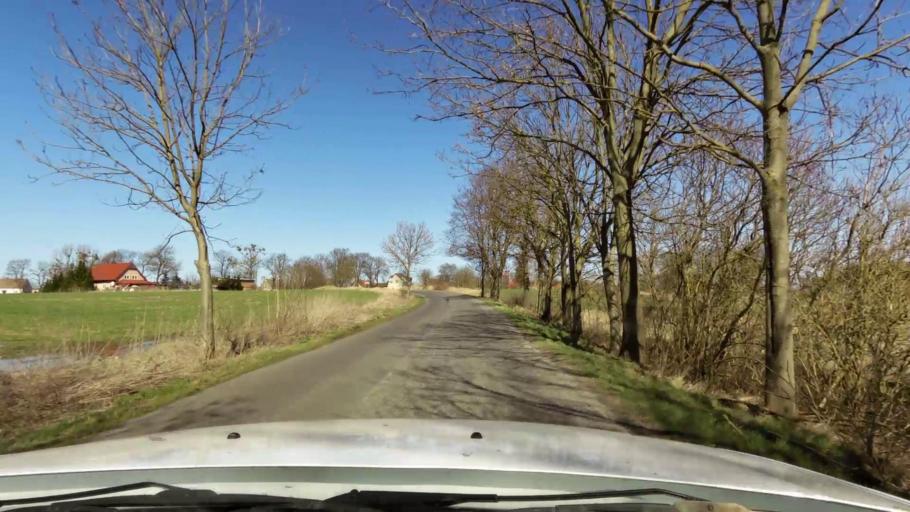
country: PL
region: West Pomeranian Voivodeship
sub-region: Powiat gryfinski
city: Cedynia
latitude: 52.8823
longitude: 14.2866
